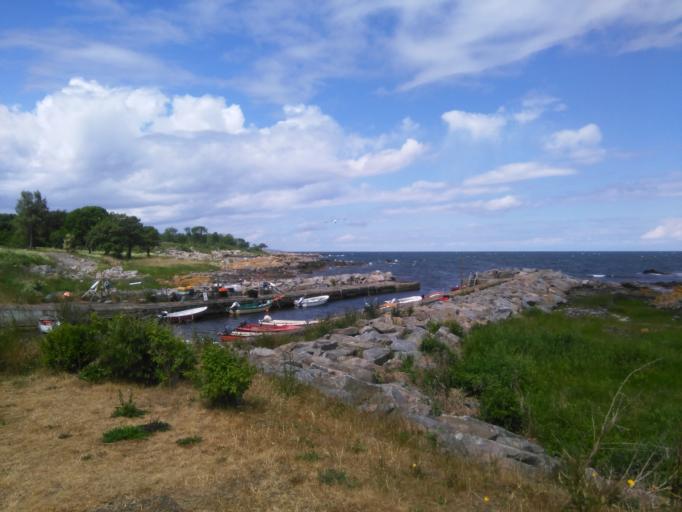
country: DK
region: Capital Region
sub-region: Bornholm Kommune
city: Nexo
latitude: 55.1545
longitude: 15.0773
